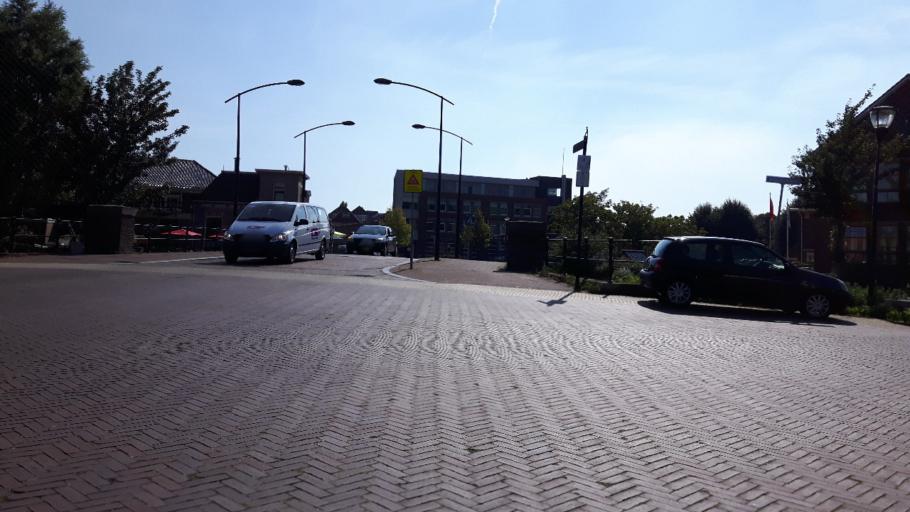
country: NL
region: Friesland
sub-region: Gemeente Franekeradeel
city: Franeker
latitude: 53.1892
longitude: 5.5408
